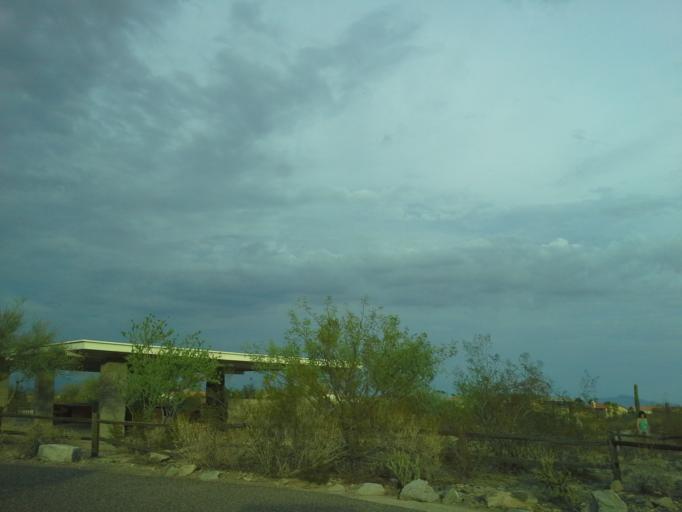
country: US
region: Arizona
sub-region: Maricopa County
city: Guadalupe
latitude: 33.3625
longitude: -111.9855
